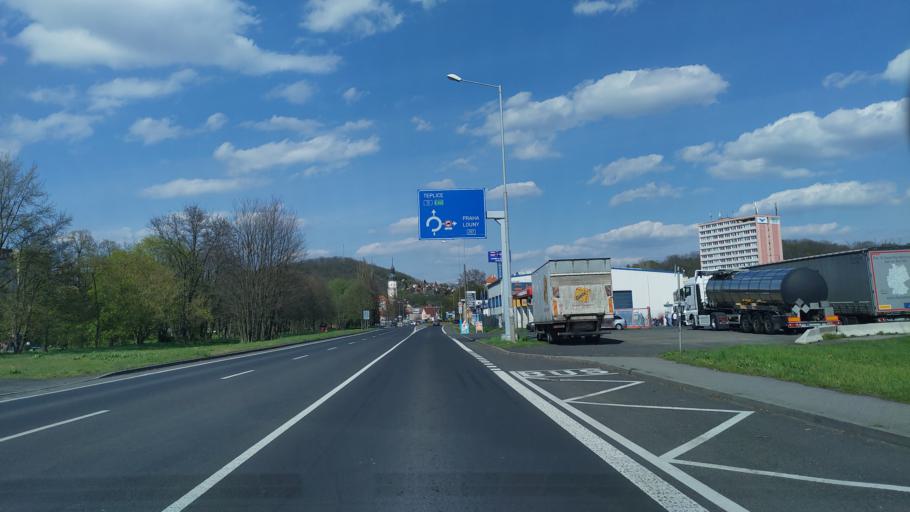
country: CZ
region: Ustecky
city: Bilina Kyselka
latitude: 50.5447
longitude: 13.7679
